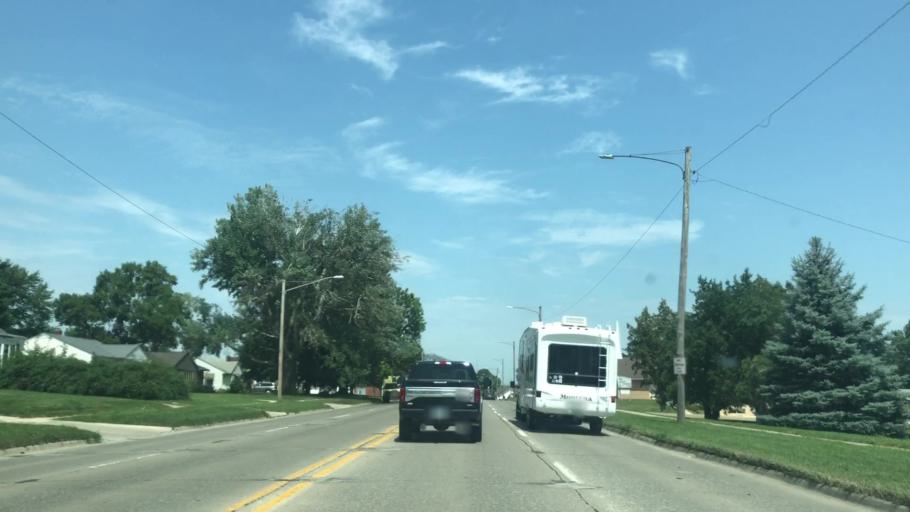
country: US
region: Iowa
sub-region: Marshall County
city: Marshalltown
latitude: 42.0307
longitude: -92.9127
